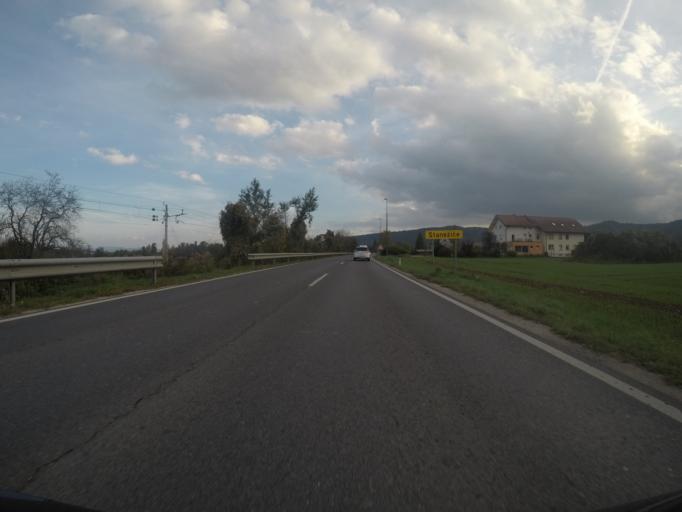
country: SI
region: Medvode
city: Zgornje Pirnice
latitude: 46.1178
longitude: 14.4412
